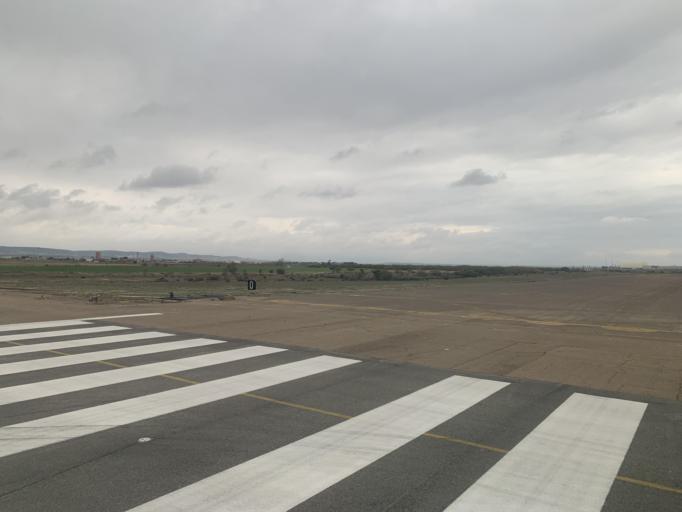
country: ES
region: Aragon
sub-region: Provincia de Zaragoza
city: Utebo
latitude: 41.6691
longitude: -1.0395
